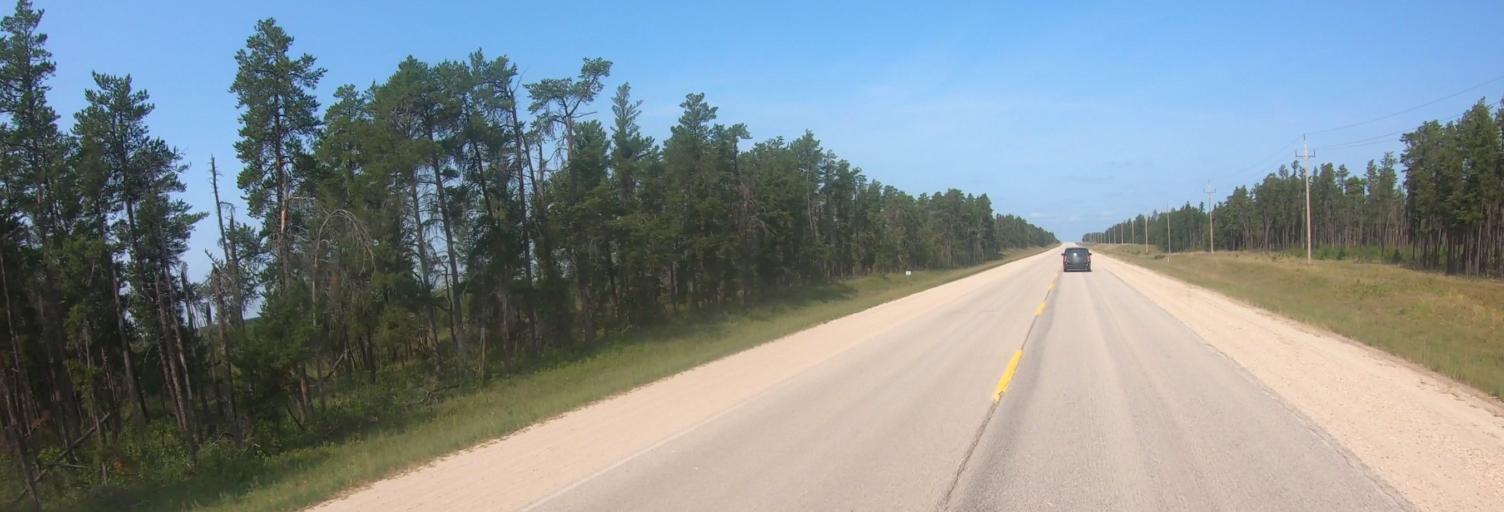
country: US
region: Minnesota
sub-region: Roseau County
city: Roseau
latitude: 49.1267
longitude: -96.0711
